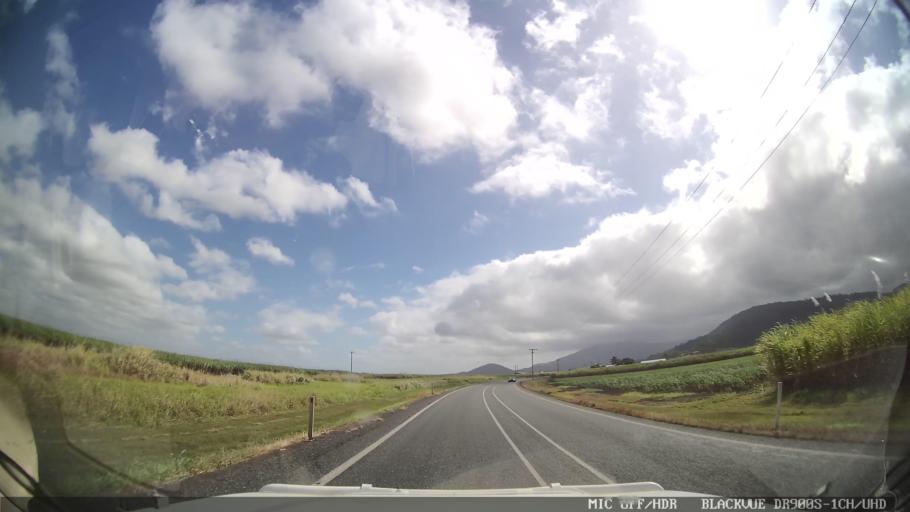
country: AU
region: Queensland
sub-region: Whitsunday
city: Red Hill
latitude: -20.3462
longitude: 148.5531
